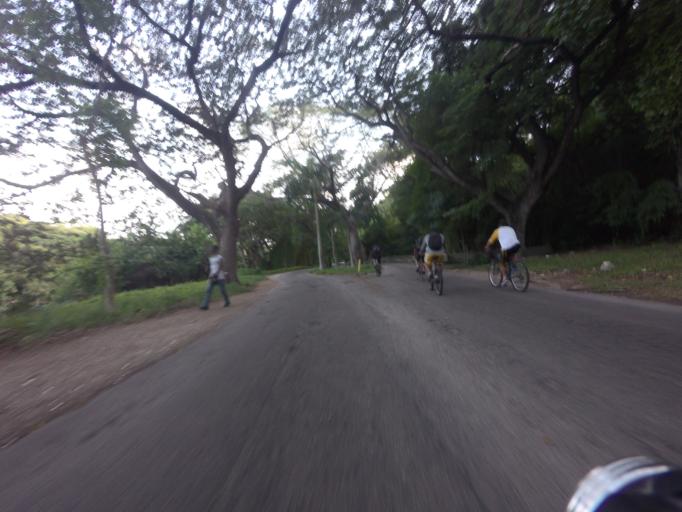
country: CU
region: La Habana
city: Cerro
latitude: 23.1142
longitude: -82.4068
